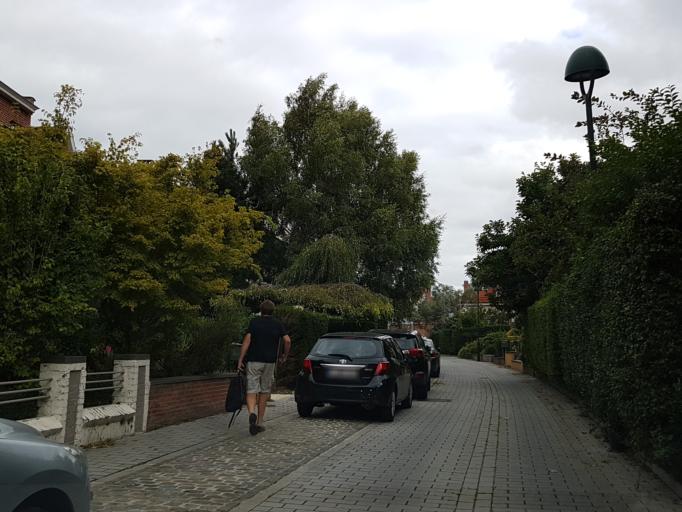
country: BE
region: Brussels Capital
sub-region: Bruxelles-Capitale
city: Brussels
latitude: 50.8659
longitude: 4.3935
